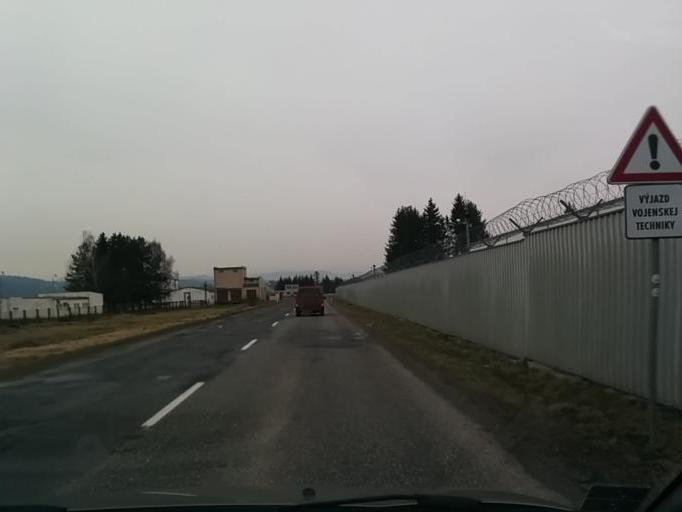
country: SK
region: Banskobystricky
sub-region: Okres Banska Bystrica
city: Zvolen
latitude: 48.6384
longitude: 19.1413
